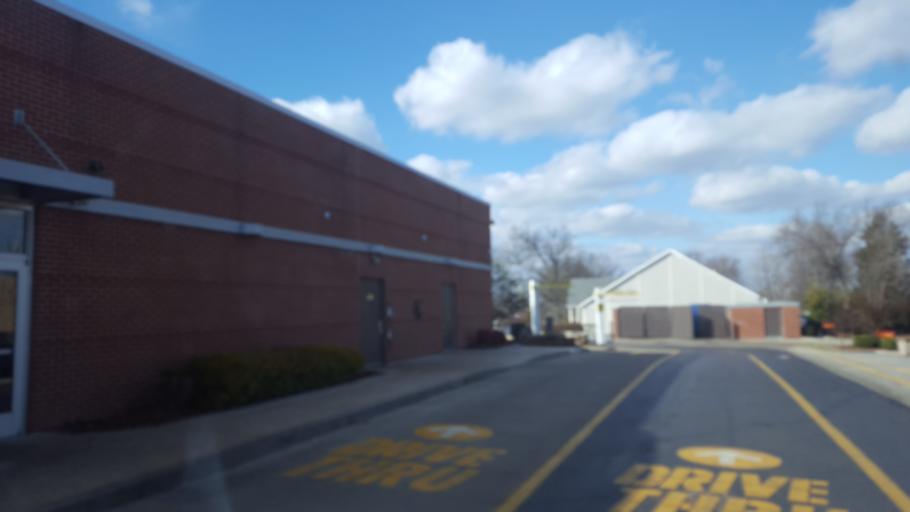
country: US
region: Kentucky
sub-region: Franklin County
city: Frankfort
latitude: 38.1981
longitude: -84.8299
